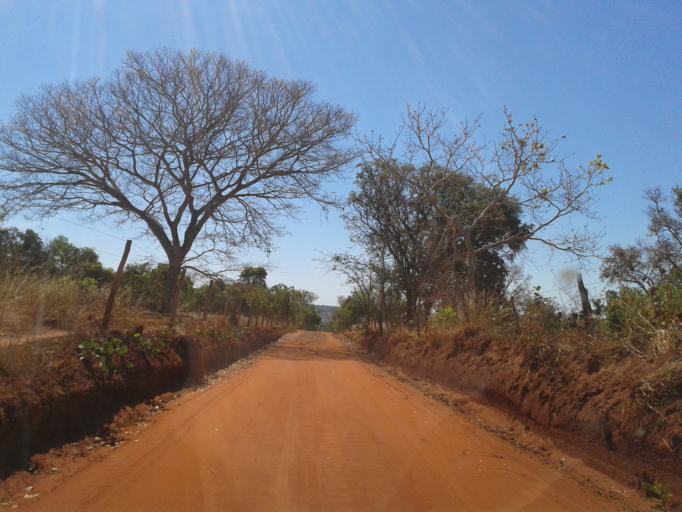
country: BR
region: Minas Gerais
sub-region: Ituiutaba
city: Ituiutaba
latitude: -19.0762
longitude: -49.3155
